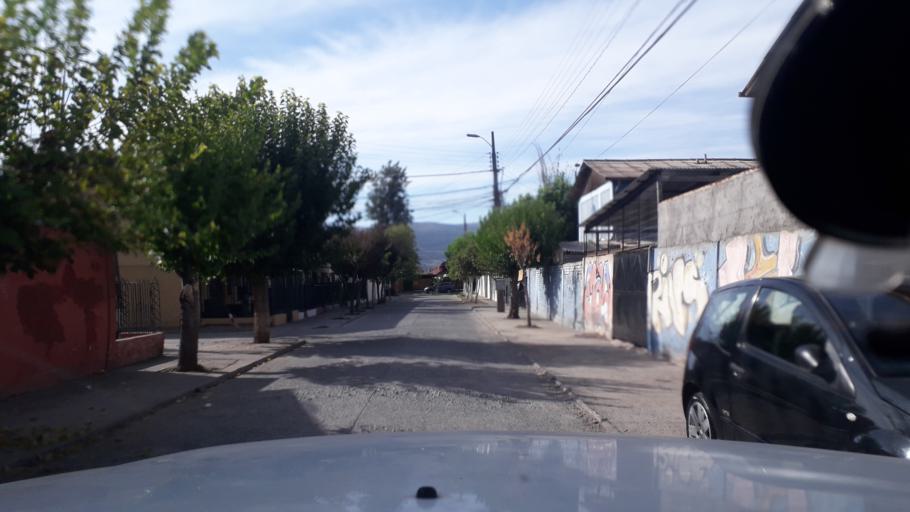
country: CL
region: Valparaiso
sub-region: Provincia de San Felipe
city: San Felipe
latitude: -32.7495
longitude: -70.7156
